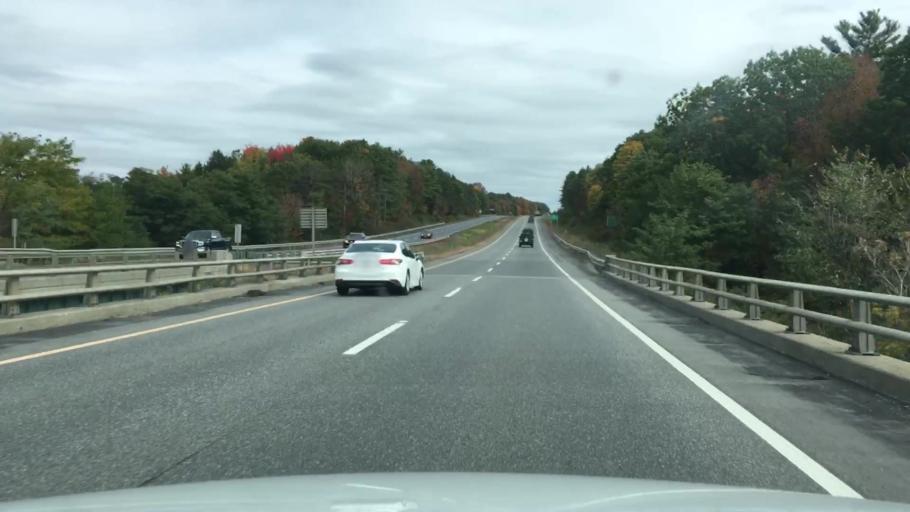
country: US
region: Maine
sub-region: Kennebec County
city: Augusta
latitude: 44.3380
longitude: -69.8073
